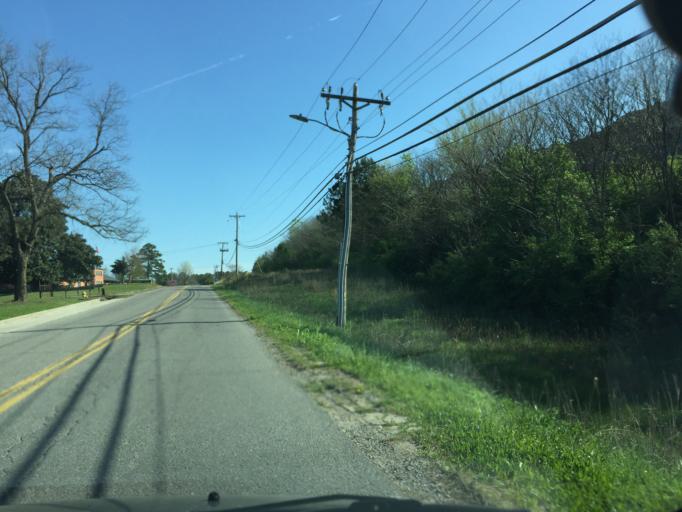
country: US
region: Tennessee
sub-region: Hamilton County
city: East Chattanooga
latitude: 35.0650
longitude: -85.2046
